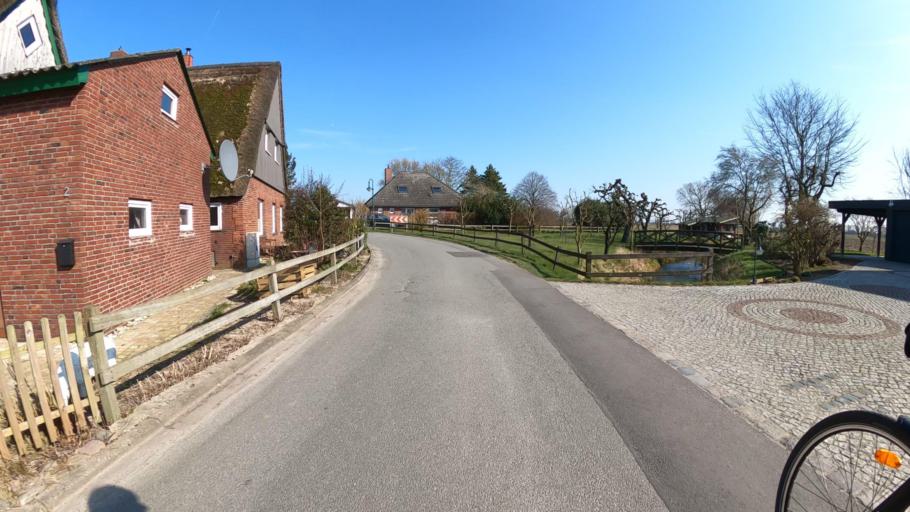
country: DE
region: Schleswig-Holstein
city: Seestermuhe
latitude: 53.6918
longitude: 9.5667
